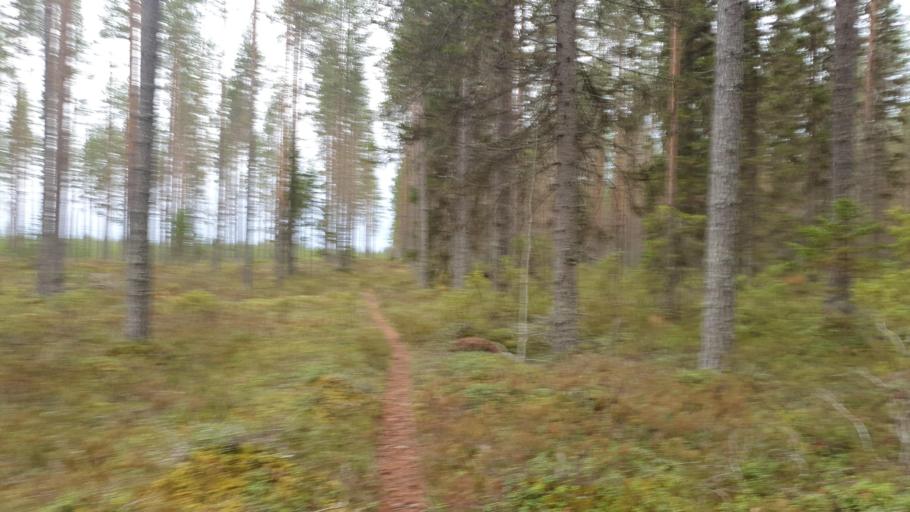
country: FI
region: Kainuu
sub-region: Kehys-Kainuu
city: Kuhmo
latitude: 64.1338
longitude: 29.3987
